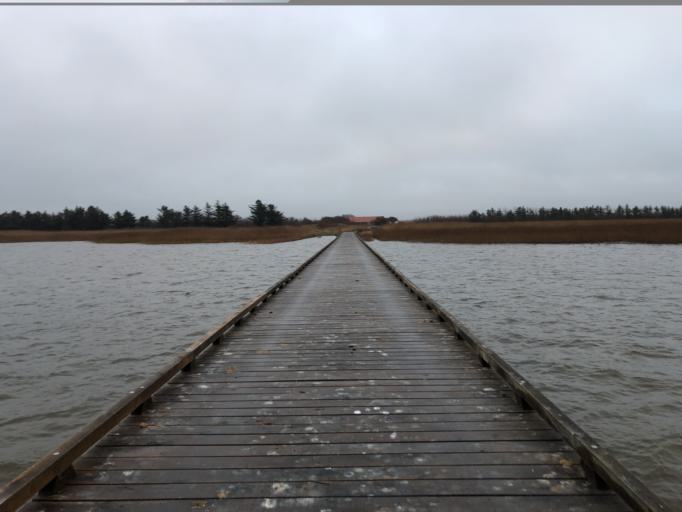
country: DK
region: Central Jutland
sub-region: Ringkobing-Skjern Kommune
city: Ringkobing
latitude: 56.1515
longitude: 8.2379
